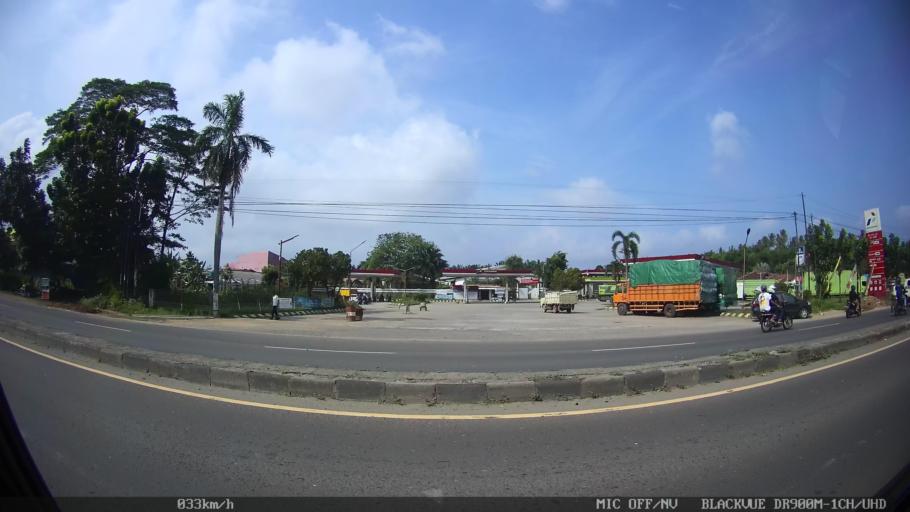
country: ID
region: Lampung
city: Kedaton
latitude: -5.3662
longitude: 105.2665
